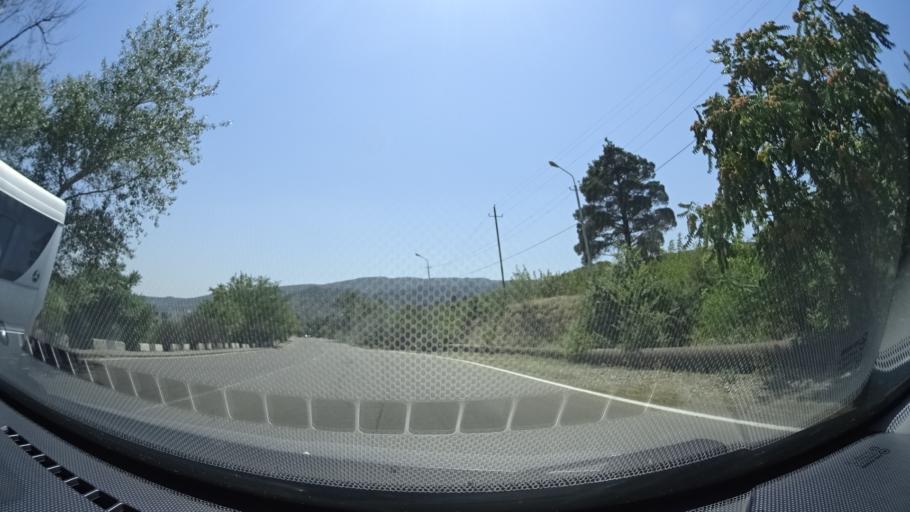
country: GE
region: Mtskheta-Mtianeti
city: Mtskheta
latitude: 41.8534
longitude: 44.7208
